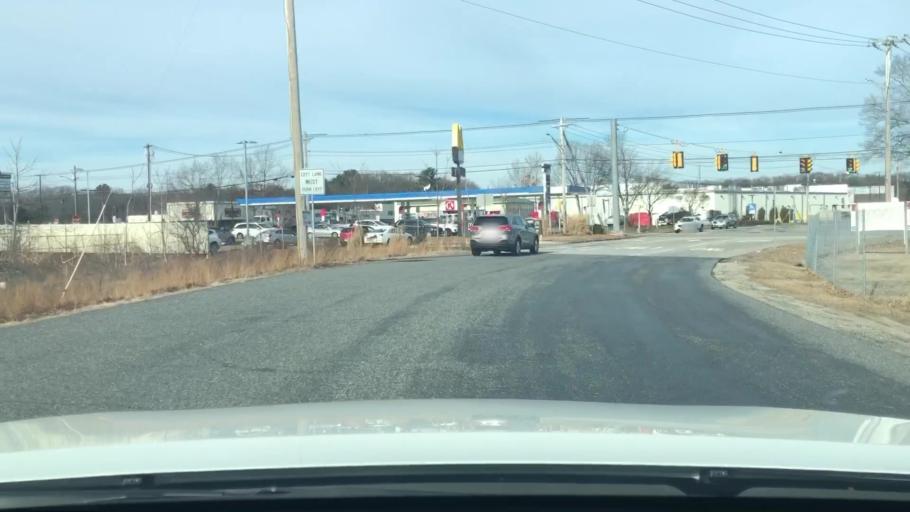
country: US
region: Massachusetts
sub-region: Worcester County
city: Milford
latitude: 42.1473
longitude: -71.4876
